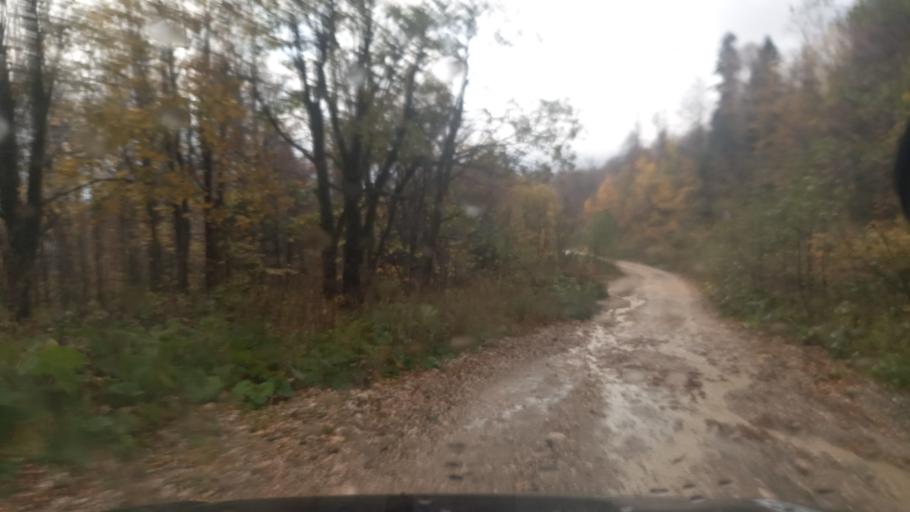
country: RU
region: Krasnodarskiy
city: Gornoye Loo
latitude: 44.0019
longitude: 39.8460
